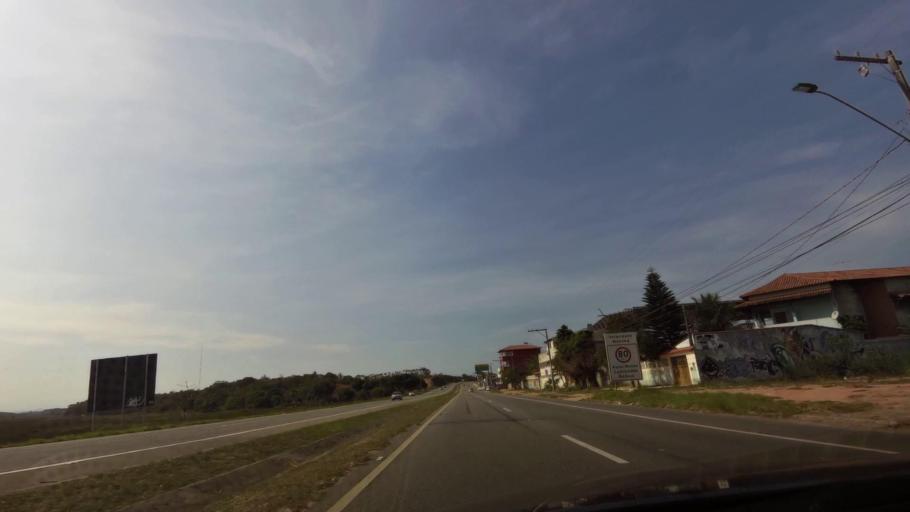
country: BR
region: Espirito Santo
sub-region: Guarapari
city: Guarapari
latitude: -20.5344
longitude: -40.3866
